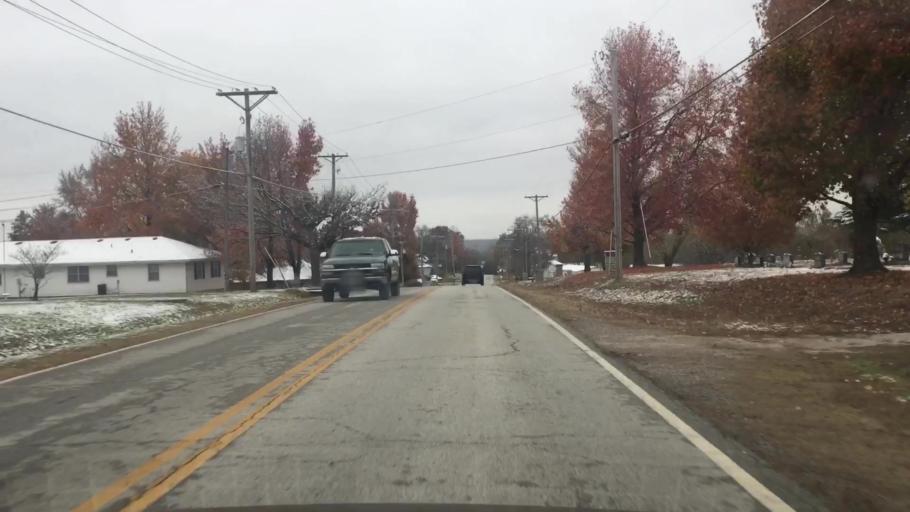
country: US
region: Missouri
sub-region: Saint Clair County
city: Osceola
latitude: 38.0381
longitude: -93.7026
